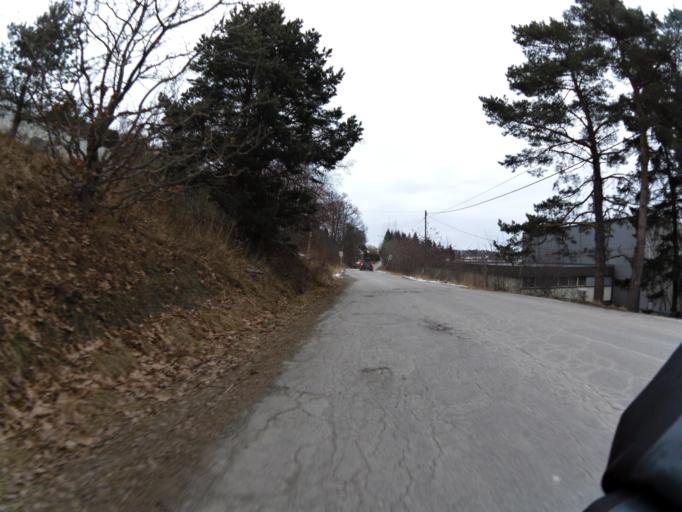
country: NO
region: Ostfold
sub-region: Fredrikstad
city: Fredrikstad
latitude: 59.2102
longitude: 10.8876
